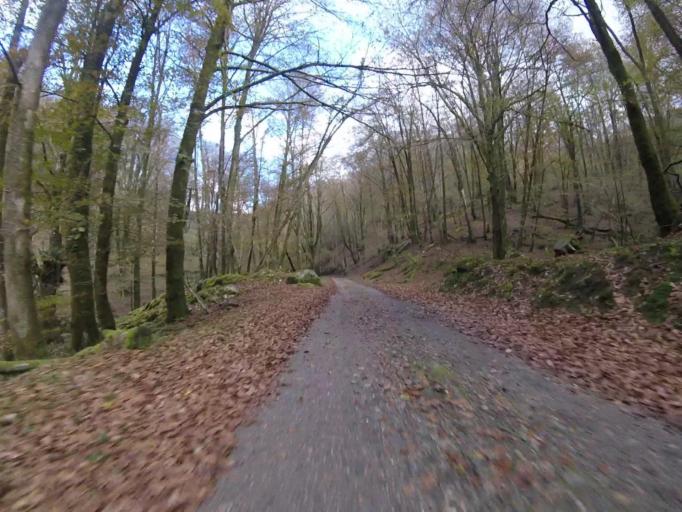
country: ES
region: Navarre
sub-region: Provincia de Navarra
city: Goizueta
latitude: 43.1990
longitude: -1.8051
